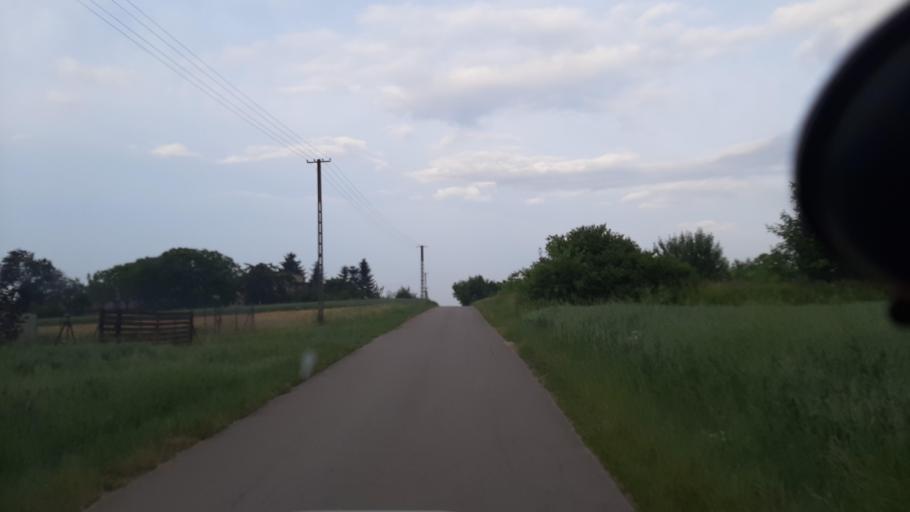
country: PL
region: Lublin Voivodeship
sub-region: Powiat lubelski
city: Garbow
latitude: 51.3533
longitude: 22.3476
